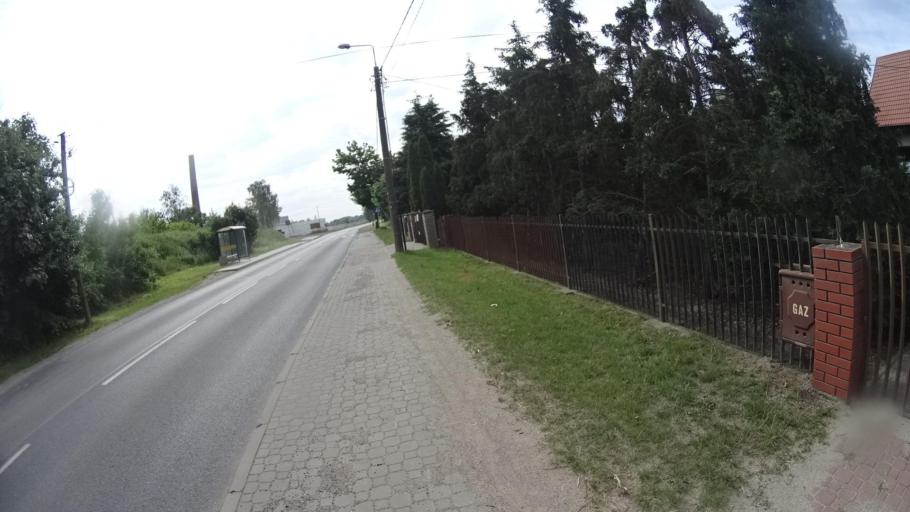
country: PL
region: Masovian Voivodeship
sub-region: Powiat warszawski zachodni
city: Jozefow
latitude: 52.1916
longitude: 20.7433
